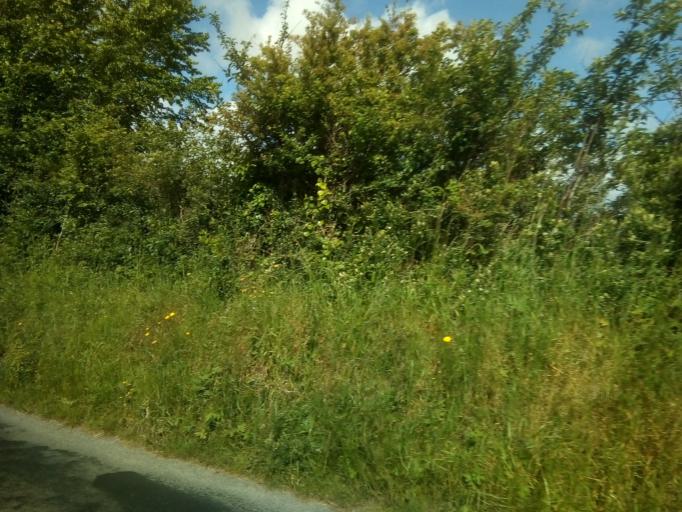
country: IE
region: Leinster
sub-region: Loch Garman
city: Loch Garman
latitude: 52.2650
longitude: -6.5578
